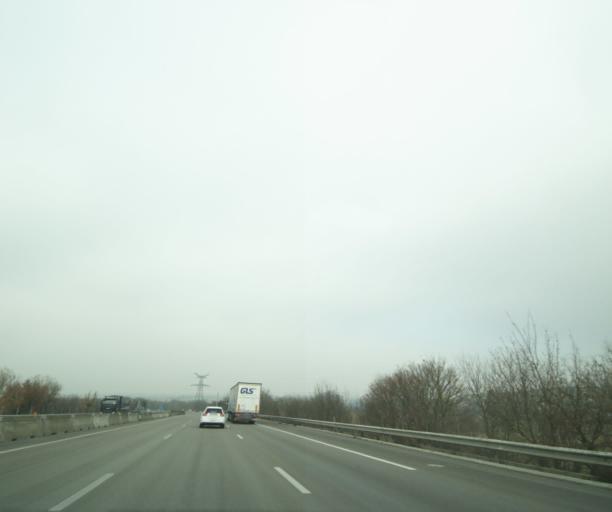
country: FR
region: Rhone-Alpes
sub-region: Departement de la Drome
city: Beausemblant
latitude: 45.2367
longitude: 4.8468
